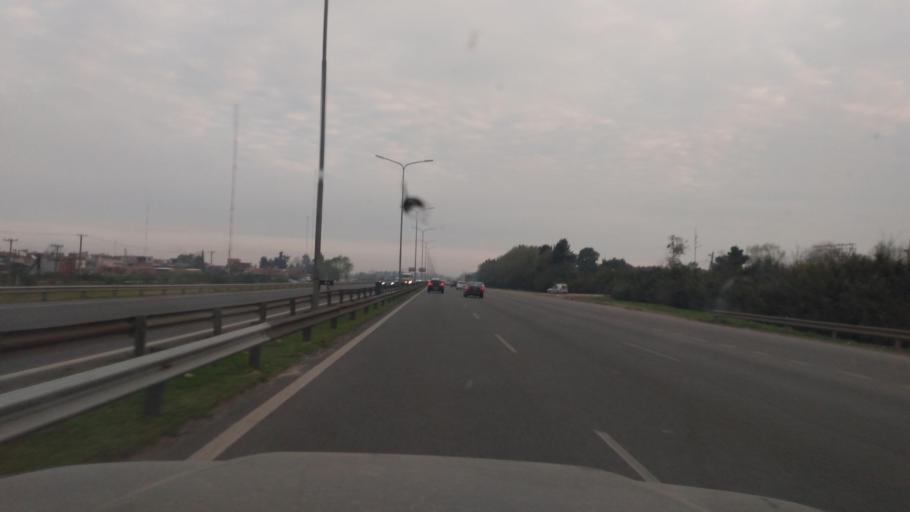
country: AR
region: Buenos Aires
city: Hurlingham
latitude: -34.5356
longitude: -58.5977
